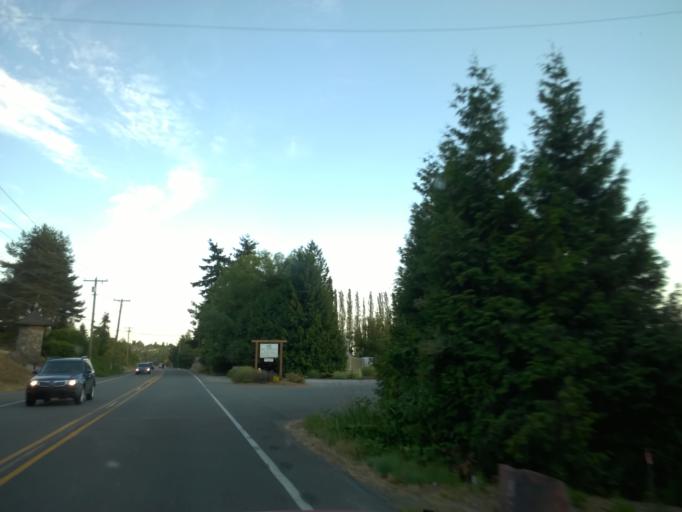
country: US
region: Washington
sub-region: King County
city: Woodinville
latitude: 47.7195
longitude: -122.1347
